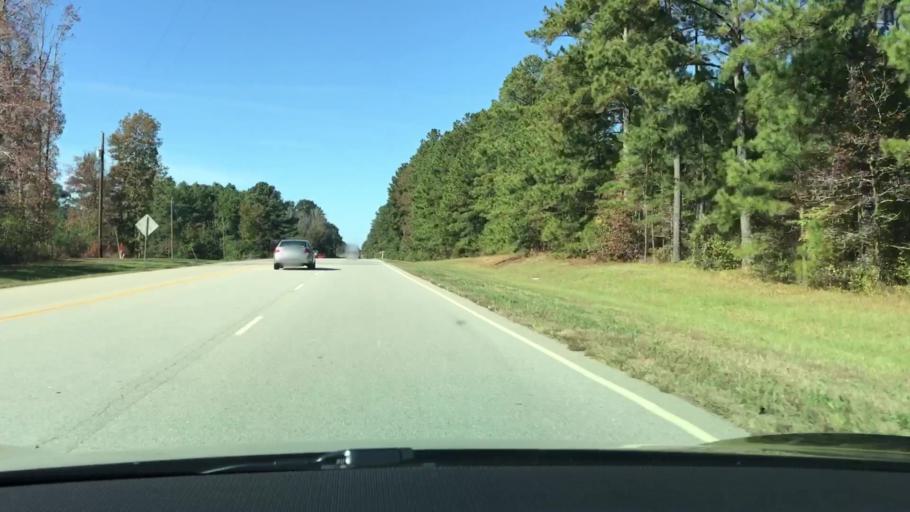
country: US
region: Georgia
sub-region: Warren County
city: Firing Range
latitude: 33.4792
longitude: -82.7397
